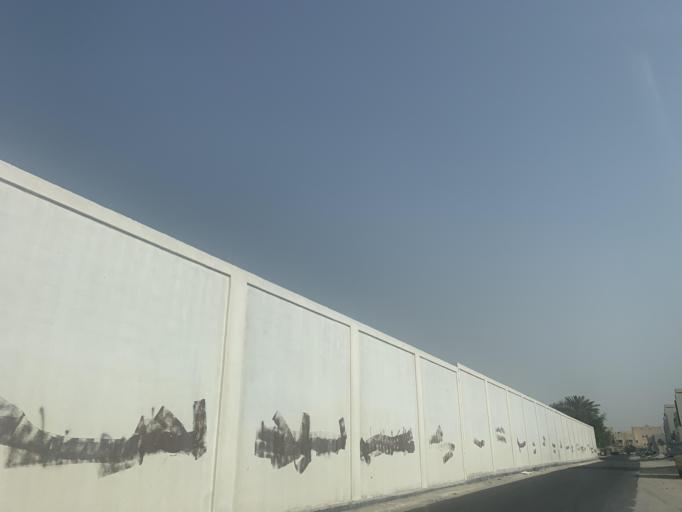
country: BH
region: Manama
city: Jidd Hafs
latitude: 26.2135
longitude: 50.4707
